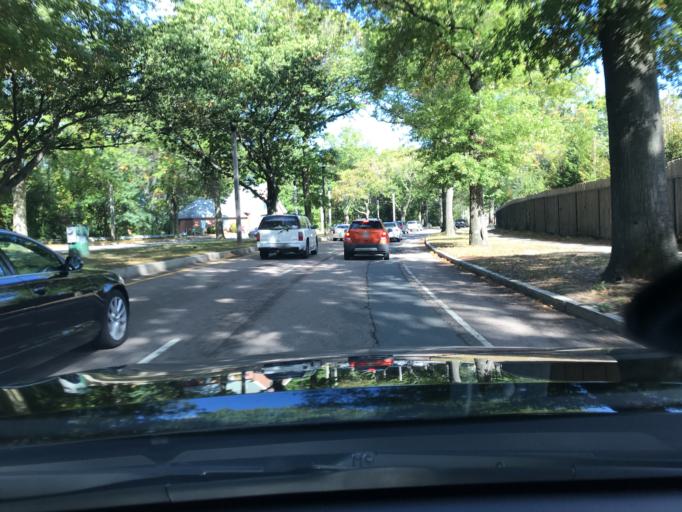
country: US
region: Massachusetts
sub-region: Norfolk County
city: Dedham
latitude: 42.2731
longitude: -71.1737
